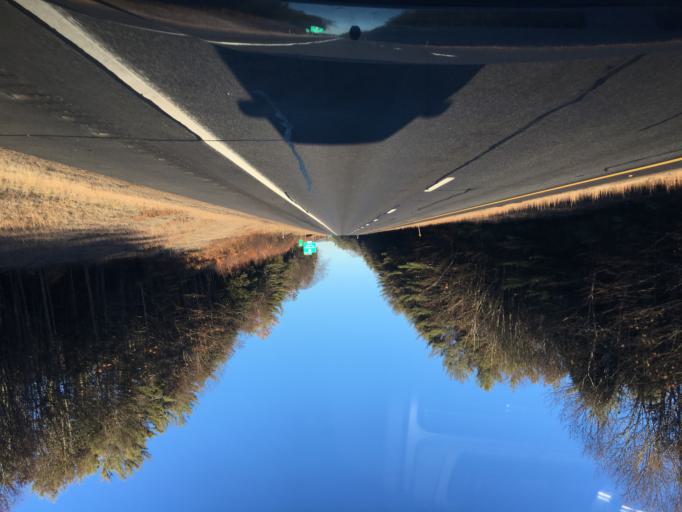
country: US
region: New Hampshire
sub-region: Belknap County
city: Sanbornton
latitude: 43.4982
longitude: -71.6072
